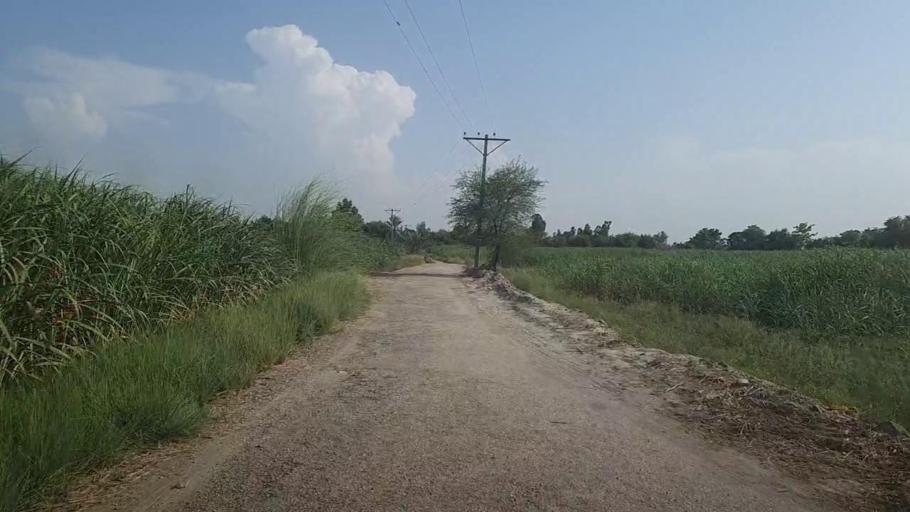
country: PK
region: Sindh
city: Ubauro
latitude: 28.1673
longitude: 69.7739
